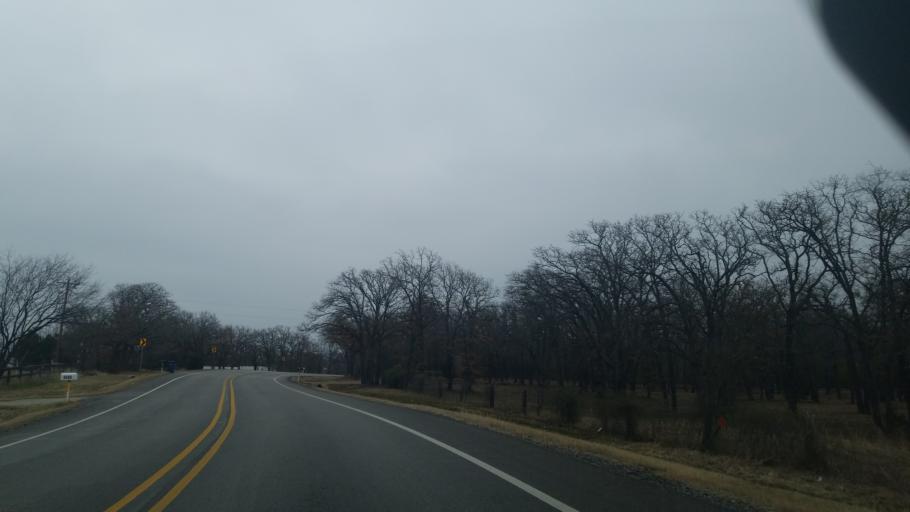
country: US
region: Texas
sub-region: Denton County
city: Argyle
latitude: 33.1325
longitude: -97.1474
